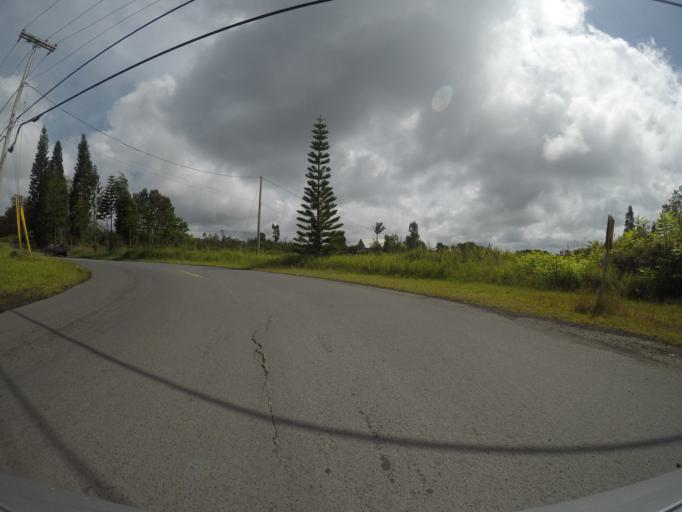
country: US
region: Hawaii
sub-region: Hawaii County
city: Fern Acres
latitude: 19.4792
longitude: -155.1420
